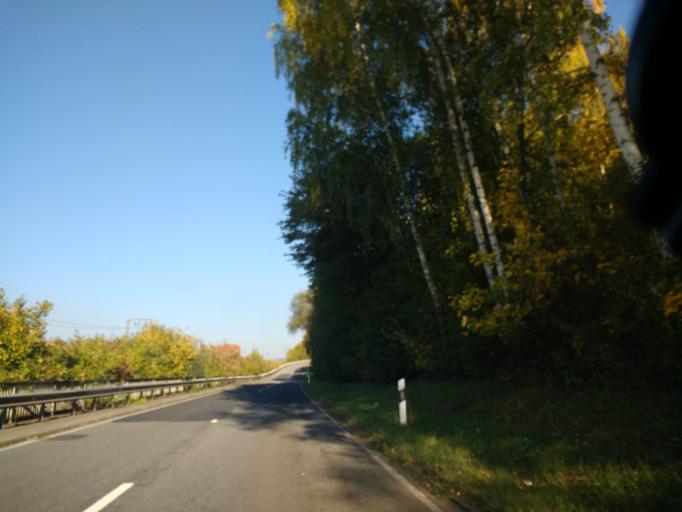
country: DE
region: Rheinland-Pfalz
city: Konz
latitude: 49.7136
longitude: 6.6025
